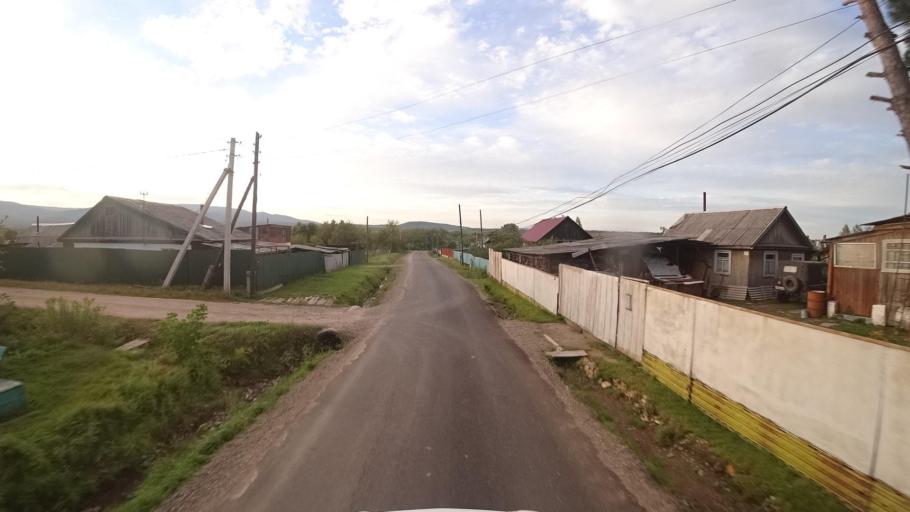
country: RU
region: Primorskiy
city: Yakovlevka
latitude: 44.4227
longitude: 133.4663
